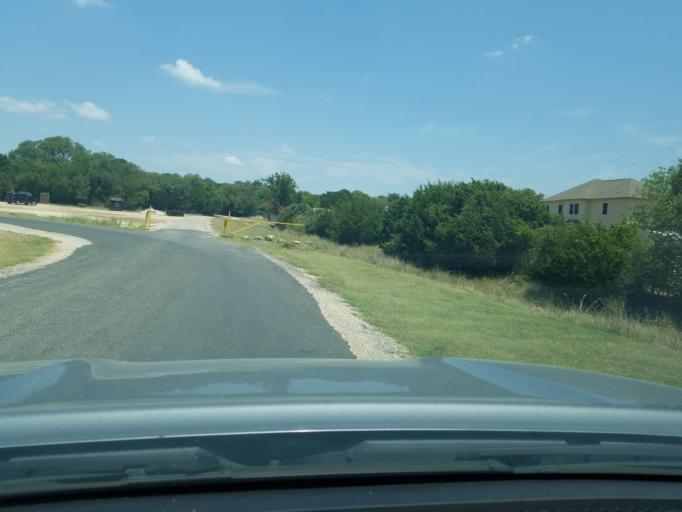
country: US
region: Texas
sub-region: Bexar County
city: Timberwood Park
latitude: 29.6964
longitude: -98.4901
